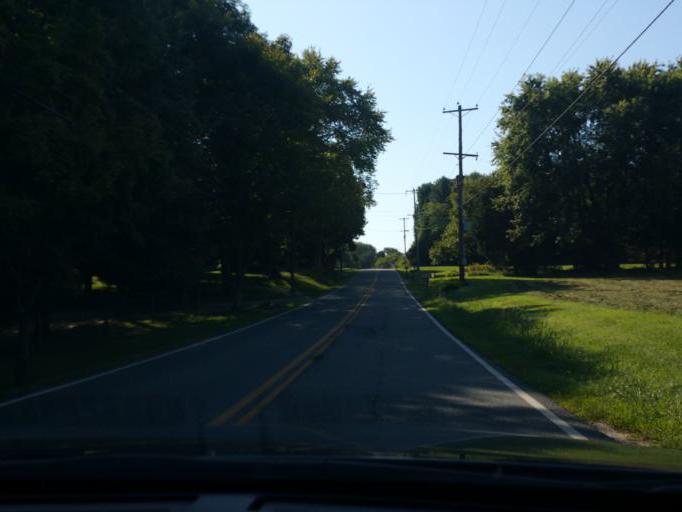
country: US
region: Maryland
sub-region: Cecil County
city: Rising Sun
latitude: 39.6520
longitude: -76.1451
